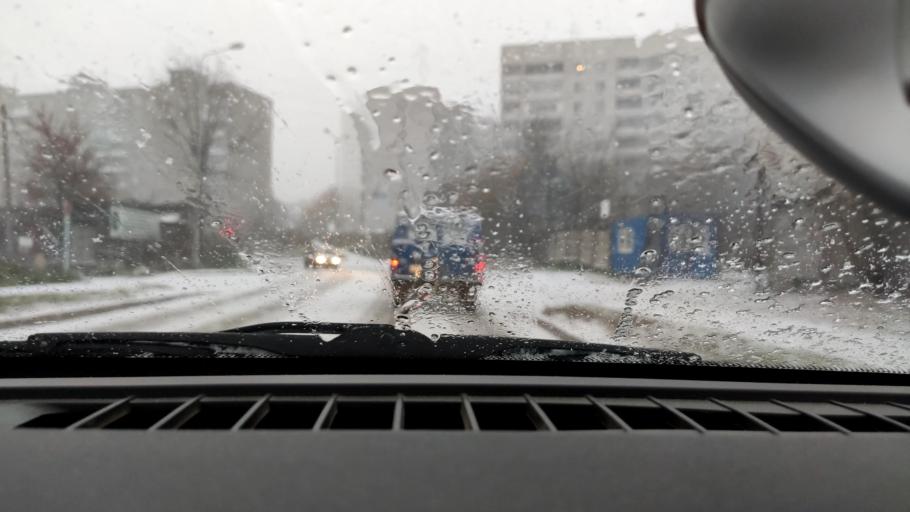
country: RU
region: Perm
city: Perm
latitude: 57.9809
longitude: 56.2801
